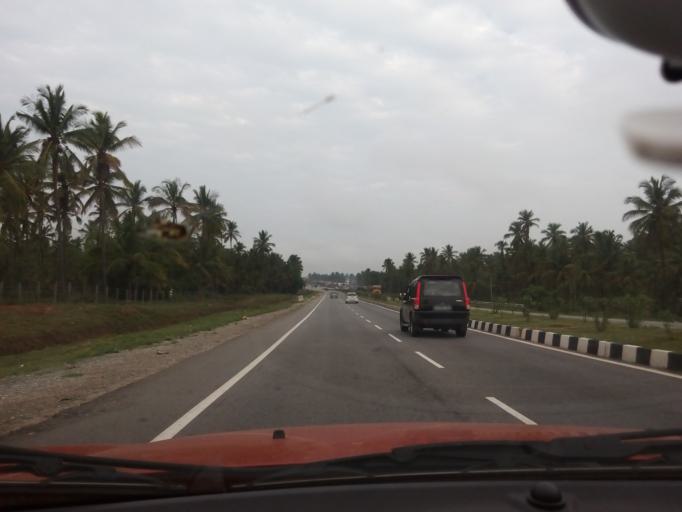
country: IN
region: Karnataka
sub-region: Mandya
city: Belluru
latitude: 12.9644
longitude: 76.6714
